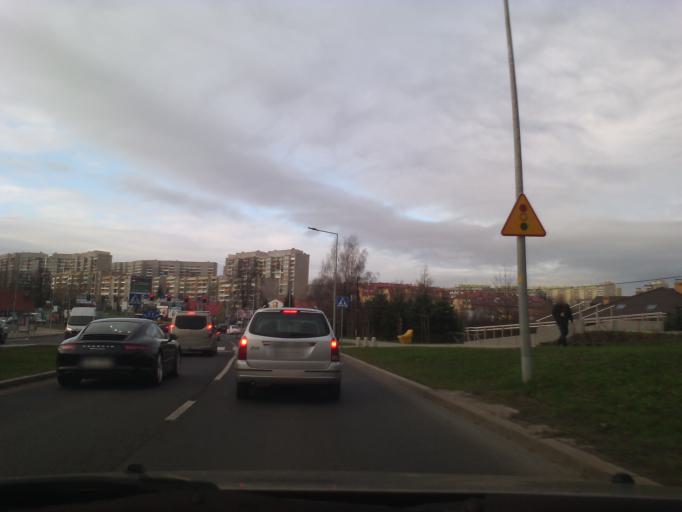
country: PL
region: Lower Silesian Voivodeship
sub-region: Powiat walbrzyski
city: Szczawno-Zdroj
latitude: 50.8258
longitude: 16.2915
